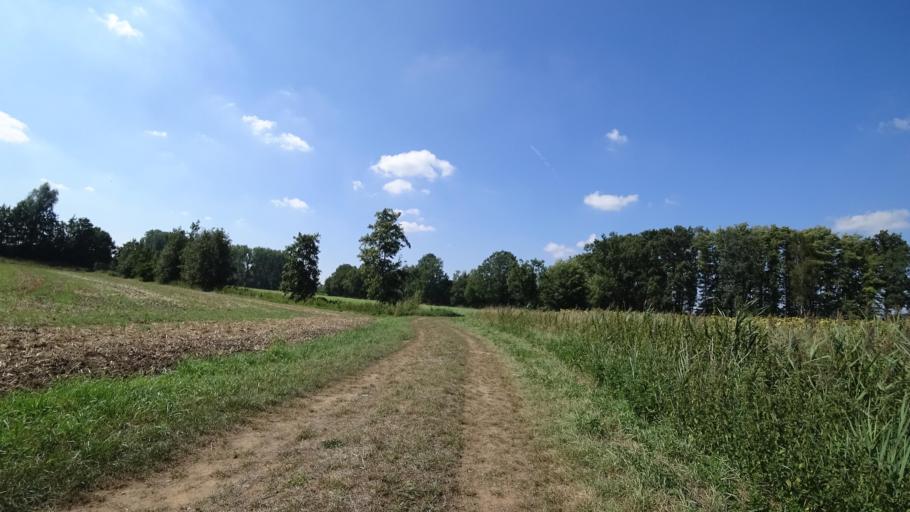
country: DE
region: North Rhine-Westphalia
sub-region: Regierungsbezirk Detmold
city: Rheda-Wiedenbruck
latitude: 51.8849
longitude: 8.3033
